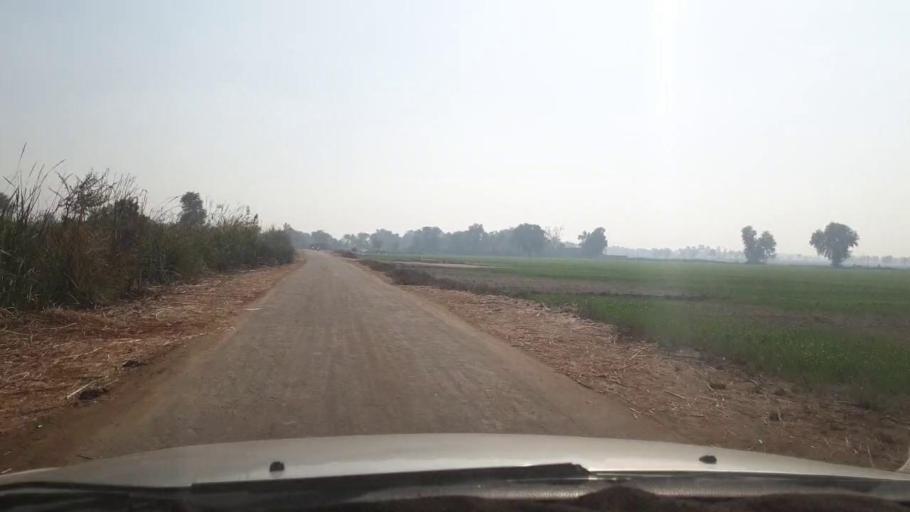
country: PK
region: Sindh
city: Khanpur
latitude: 27.7315
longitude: 69.5137
